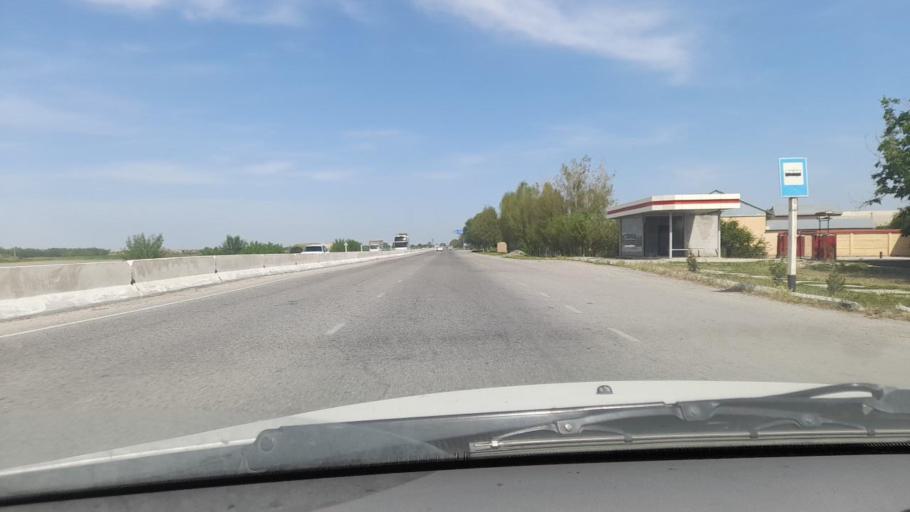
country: UZ
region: Samarqand
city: Kattaqo'rg'on
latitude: 39.9176
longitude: 66.3297
